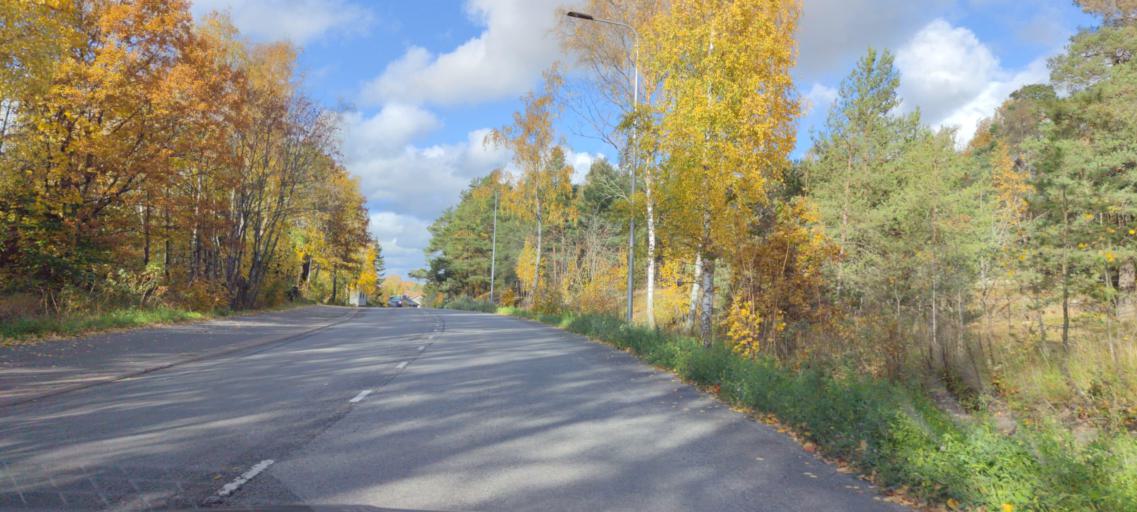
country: FI
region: Varsinais-Suomi
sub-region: Turku
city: Turku
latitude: 60.4240
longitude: 22.2702
